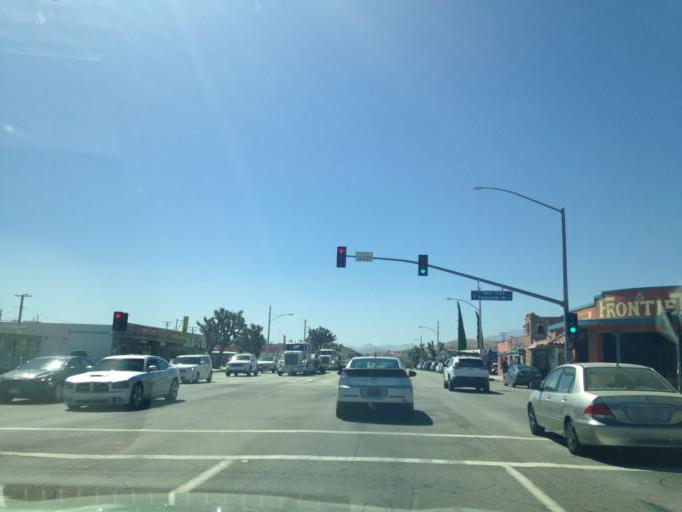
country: US
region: California
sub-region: San Bernardino County
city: Yucca Valley
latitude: 34.1196
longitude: -116.4457
